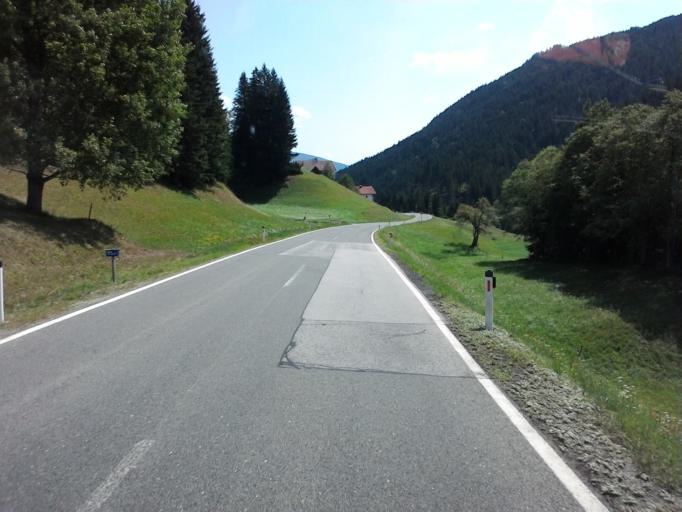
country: AT
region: Tyrol
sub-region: Politischer Bezirk Lienz
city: Untertilliach
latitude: 46.7037
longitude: 12.6844
